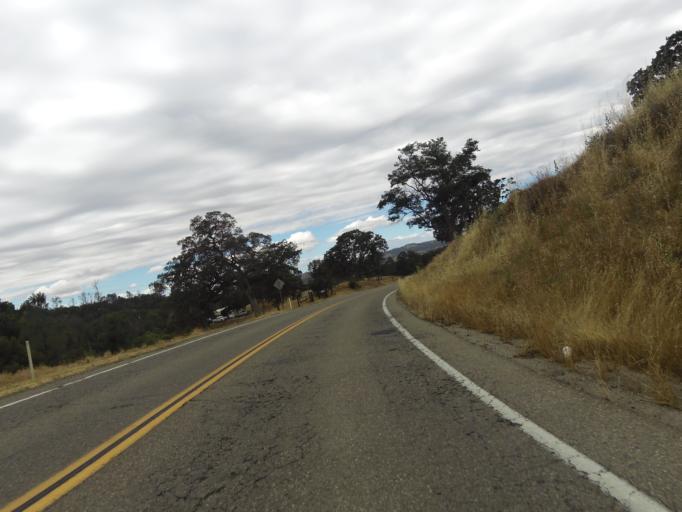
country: US
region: California
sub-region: Madera County
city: Yosemite Lakes
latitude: 37.2313
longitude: -119.7437
